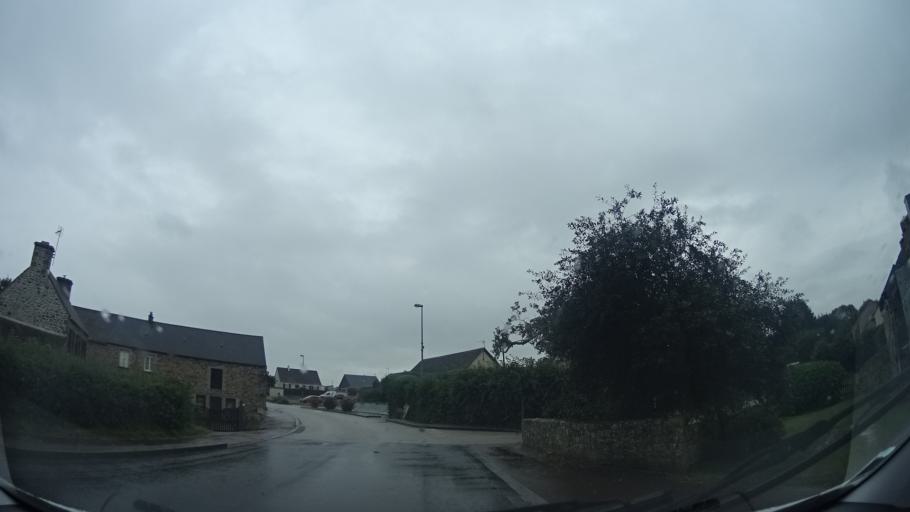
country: FR
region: Lower Normandy
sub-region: Departement de la Manche
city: Urville-Nacqueville
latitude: 49.5977
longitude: -1.7783
